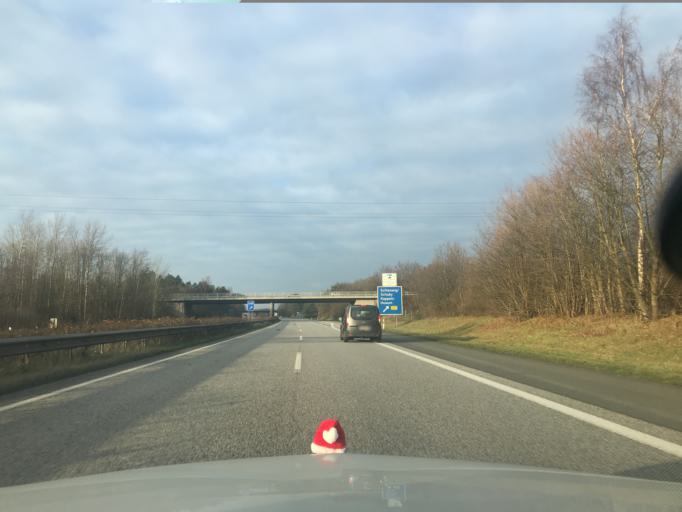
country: DE
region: Schleswig-Holstein
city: Schuby
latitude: 54.5221
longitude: 9.4905
